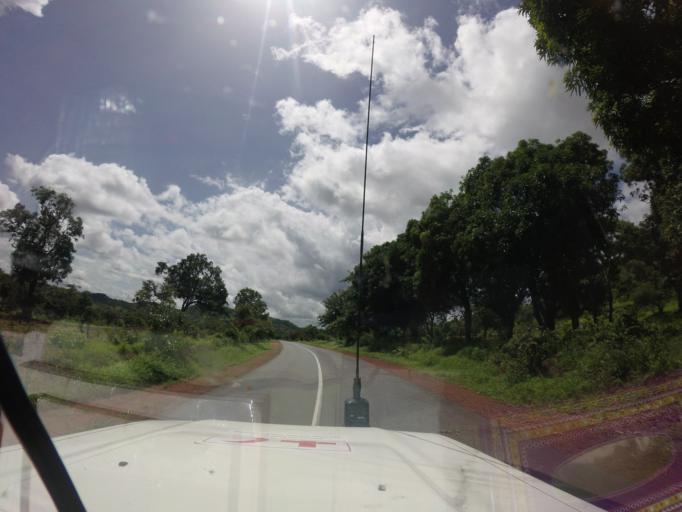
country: SL
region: Northern Province
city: Bindi
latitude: 10.1467
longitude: -11.6695
